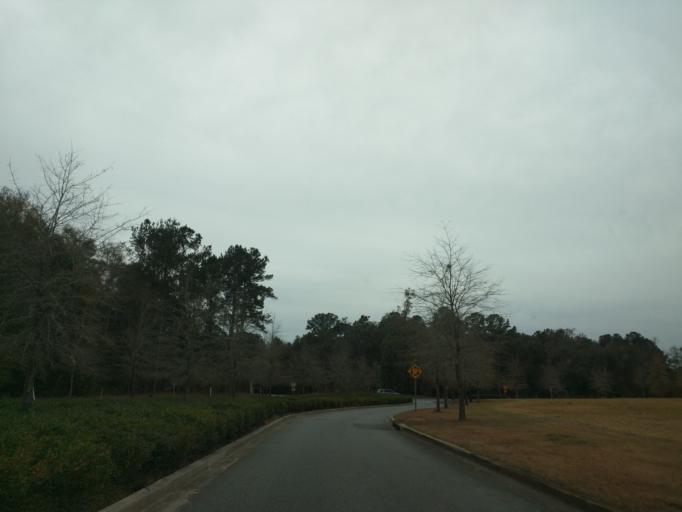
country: US
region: Florida
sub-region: Leon County
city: Tallahassee
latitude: 30.4611
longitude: -84.2098
